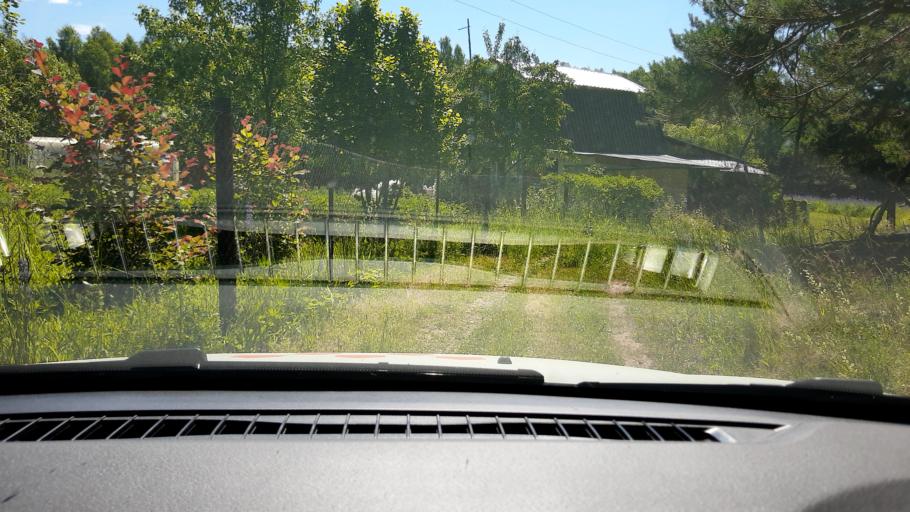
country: RU
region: Nizjnij Novgorod
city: Surovatikha
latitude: 55.8648
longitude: 43.9645
